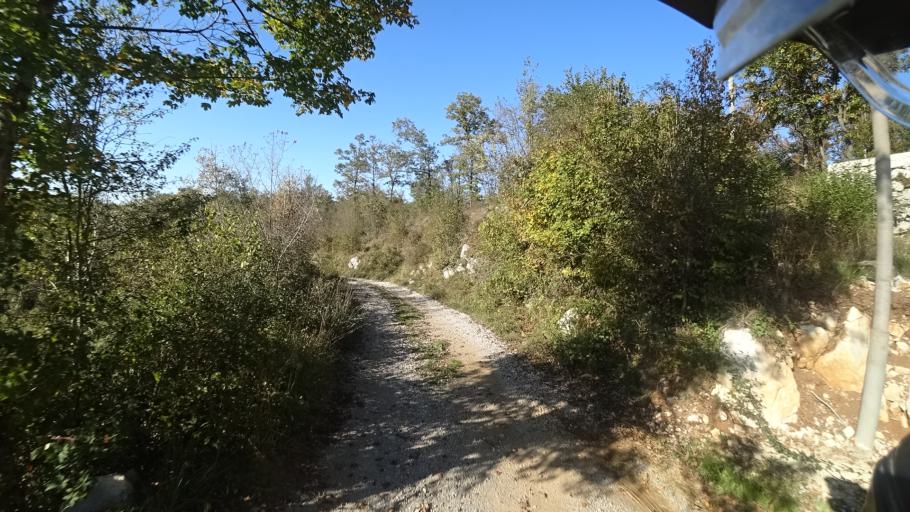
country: HR
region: Primorsko-Goranska
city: Klana
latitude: 45.4247
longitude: 14.3433
